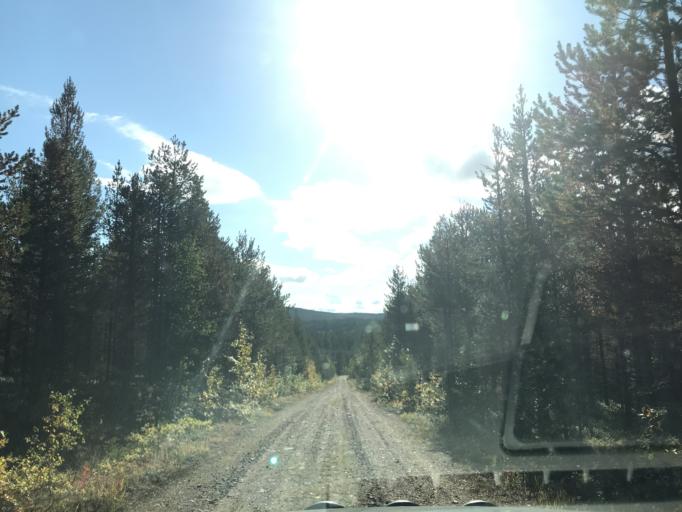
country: SE
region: Norrbotten
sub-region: Gallivare Kommun
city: Malmberget
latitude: 67.6492
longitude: 21.0825
